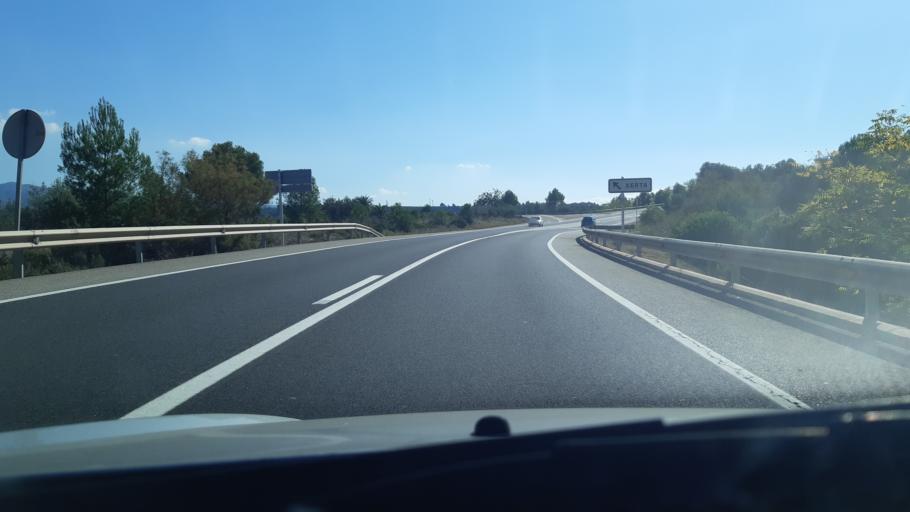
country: ES
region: Catalonia
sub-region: Provincia de Tarragona
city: Tivenys
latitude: 40.9184
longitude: 0.4937
